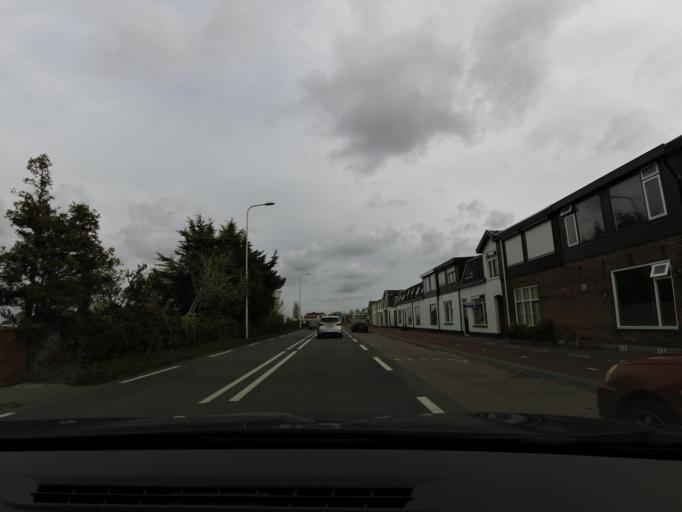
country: NL
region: South Holland
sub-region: Gemeente Noordwijkerhout
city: Noordwijkerhout
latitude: 52.2409
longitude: 4.5017
